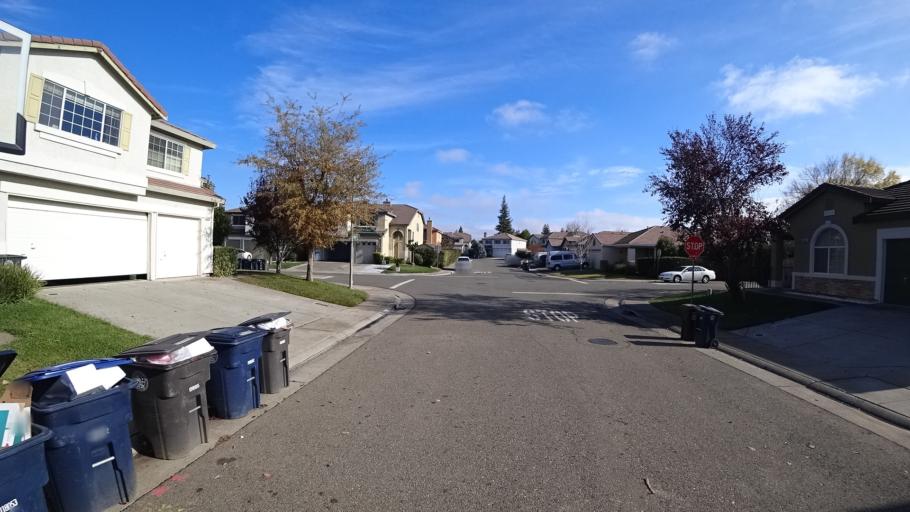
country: US
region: California
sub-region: Sacramento County
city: Antelope
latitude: 38.6896
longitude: -121.3114
